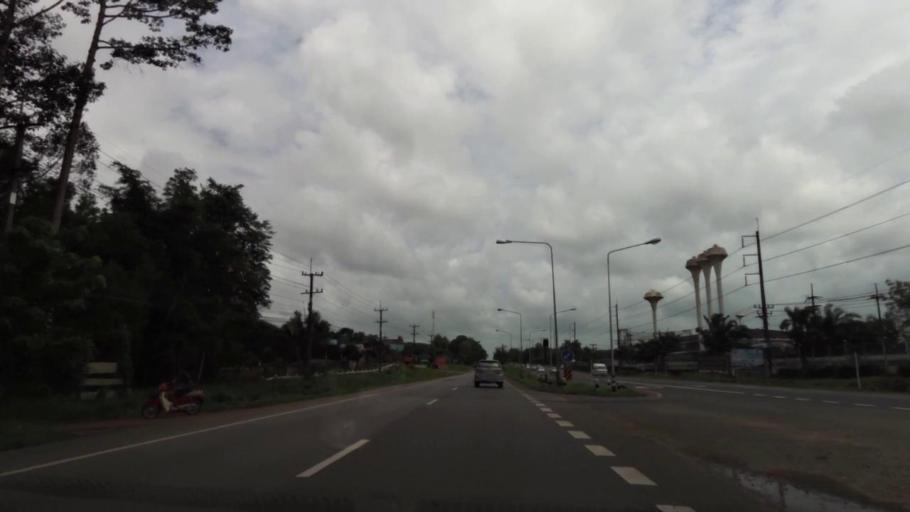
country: TH
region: Chanthaburi
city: Na Yai Am
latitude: 12.7436
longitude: 101.8872
